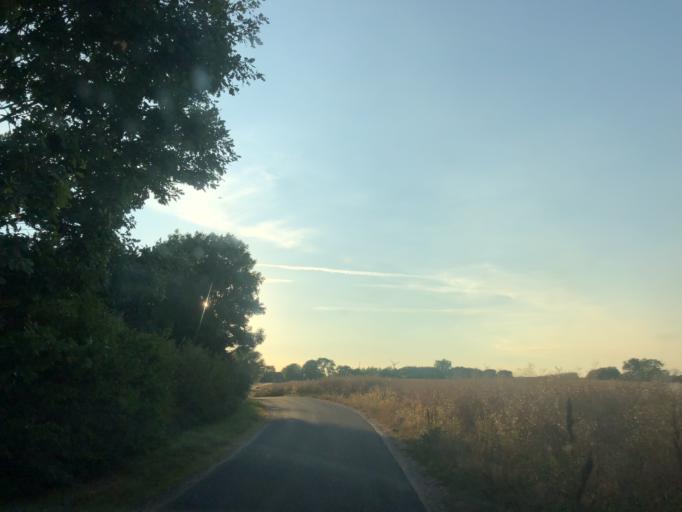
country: DK
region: Central Jutland
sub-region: Holstebro Kommune
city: Holstebro
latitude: 56.3692
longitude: 8.6802
